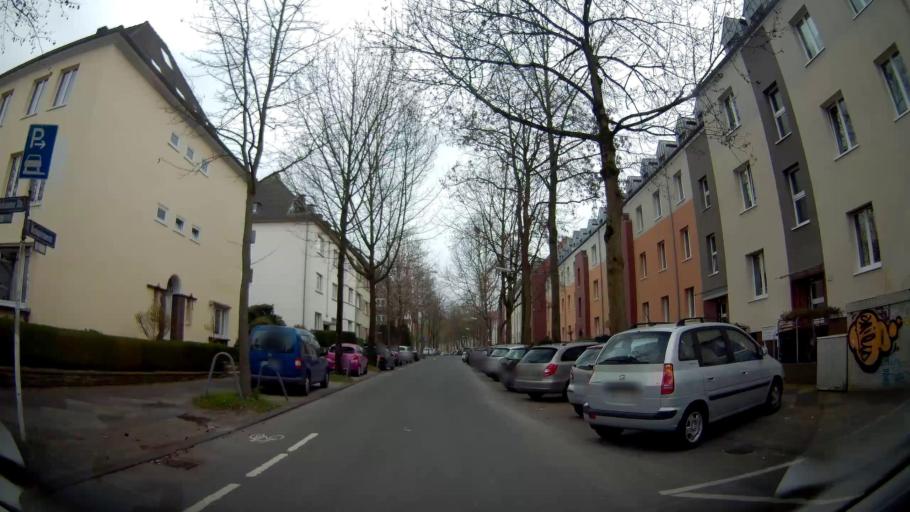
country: DE
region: North Rhine-Westphalia
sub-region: Regierungsbezirk Arnsberg
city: Dortmund
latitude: 51.5098
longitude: 7.4842
